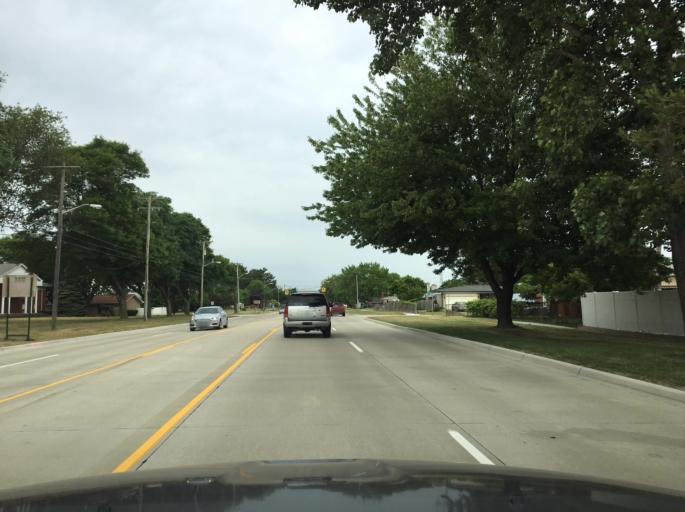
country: US
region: Michigan
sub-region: Macomb County
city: Fraser
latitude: 42.5227
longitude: -82.9782
